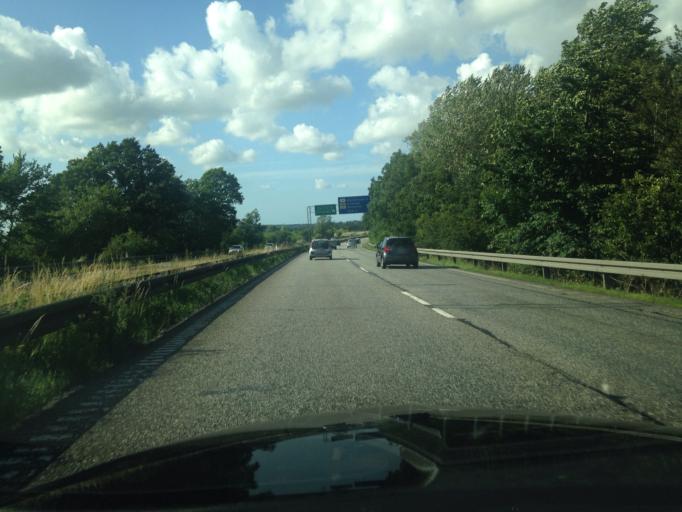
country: DK
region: Capital Region
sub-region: Horsholm Kommune
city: Horsholm
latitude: 55.8672
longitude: 12.4840
